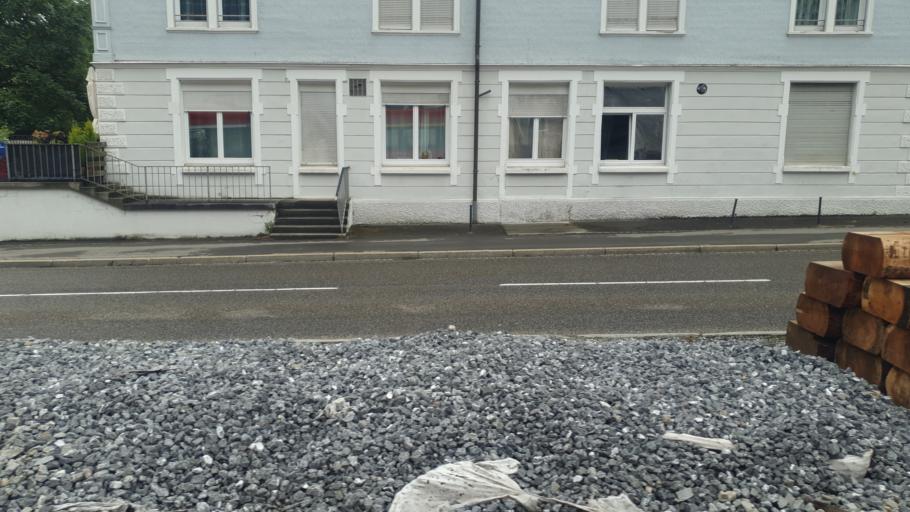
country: CH
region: Saint Gallen
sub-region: Wahlkreis St. Gallen
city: Sankt Gallen
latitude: 47.4078
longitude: 9.3693
